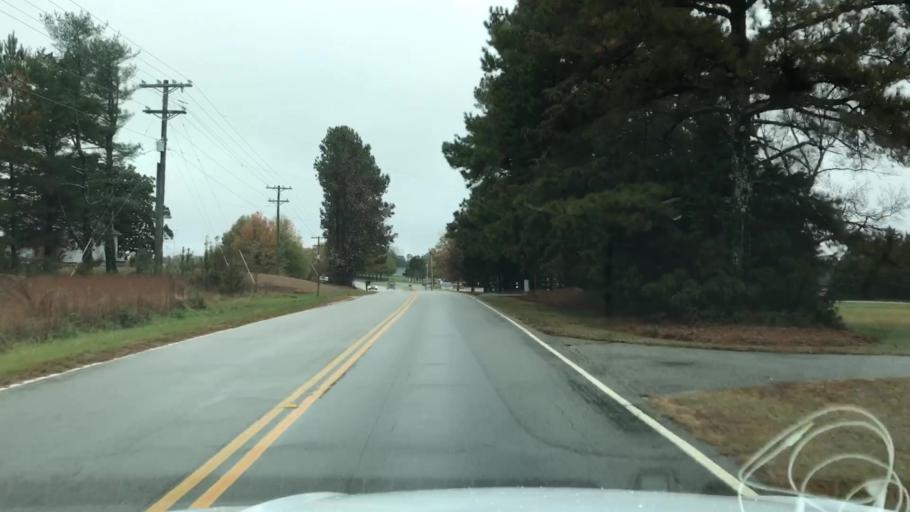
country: US
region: South Carolina
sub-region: Spartanburg County
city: Roebuck
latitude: 34.8048
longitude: -81.9174
